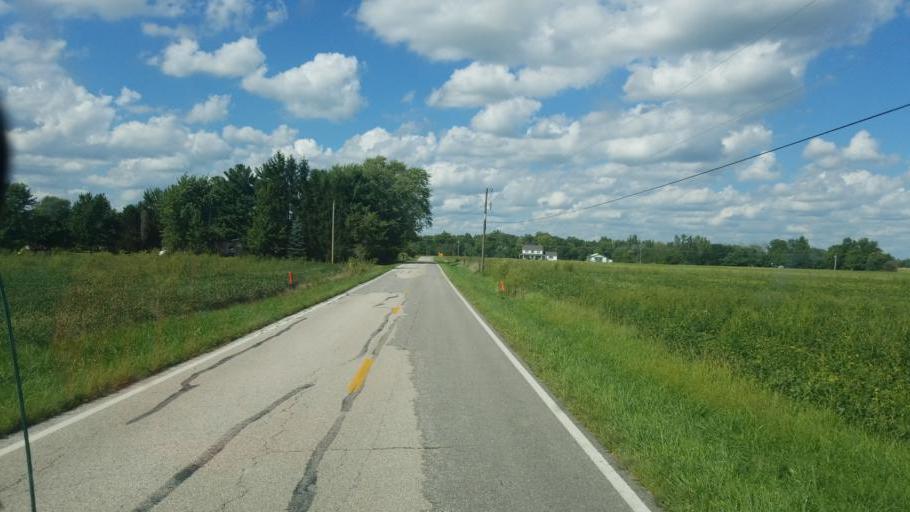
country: US
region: Ohio
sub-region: Union County
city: Richwood
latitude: 40.3344
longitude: -83.2381
